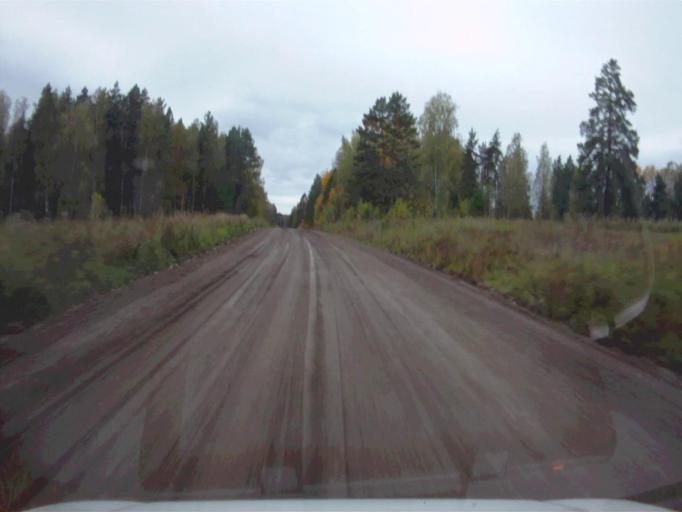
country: RU
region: Chelyabinsk
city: Nyazepetrovsk
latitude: 56.0914
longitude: 59.4123
